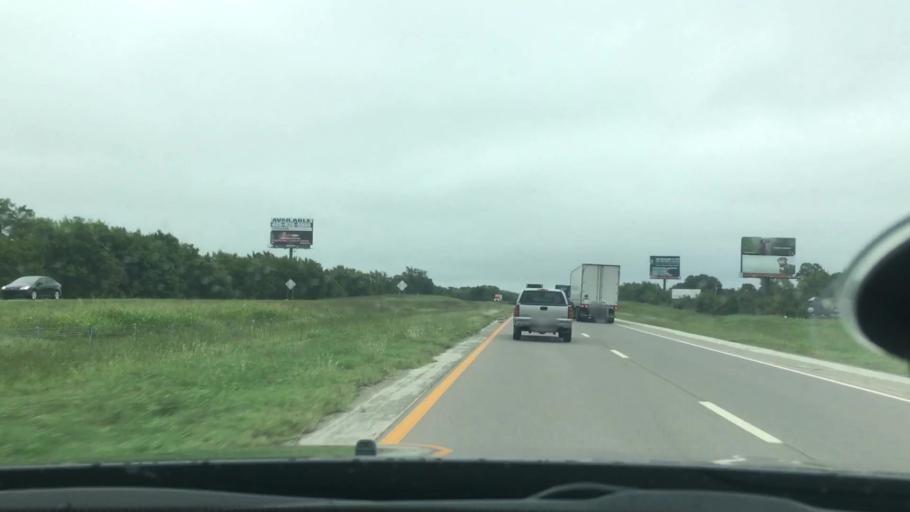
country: US
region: Oklahoma
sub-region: Okfuskee County
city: Okemah
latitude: 35.4284
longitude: -96.2455
